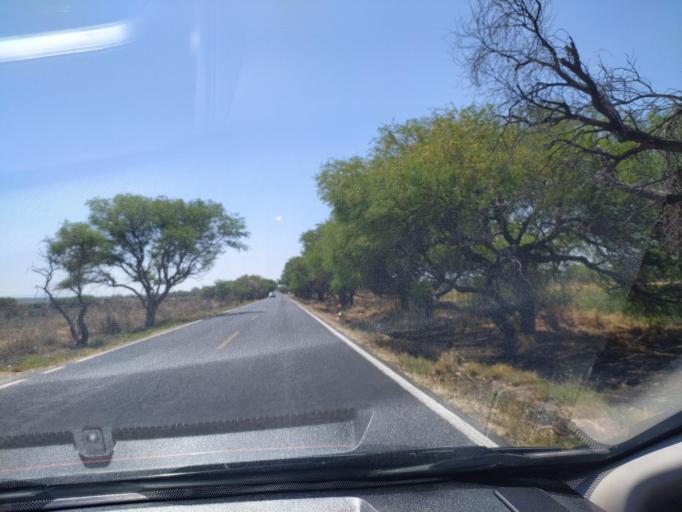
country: MX
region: Guanajuato
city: San Roque
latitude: 20.9588
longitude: -101.8489
